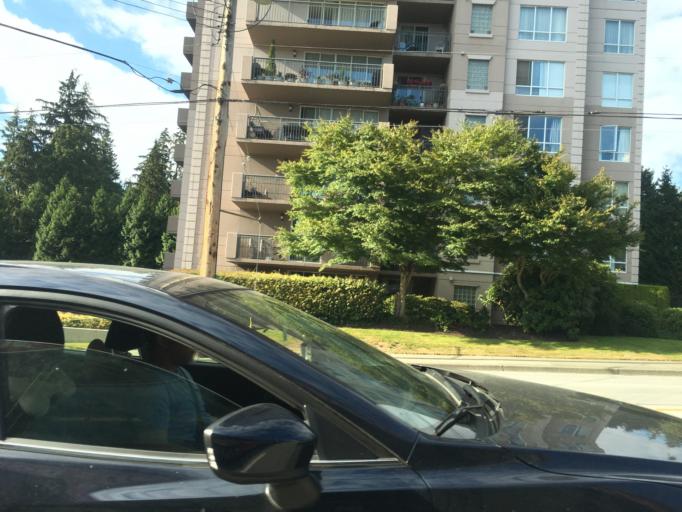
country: CA
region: British Columbia
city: New Westminster
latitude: 49.2491
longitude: -122.8886
